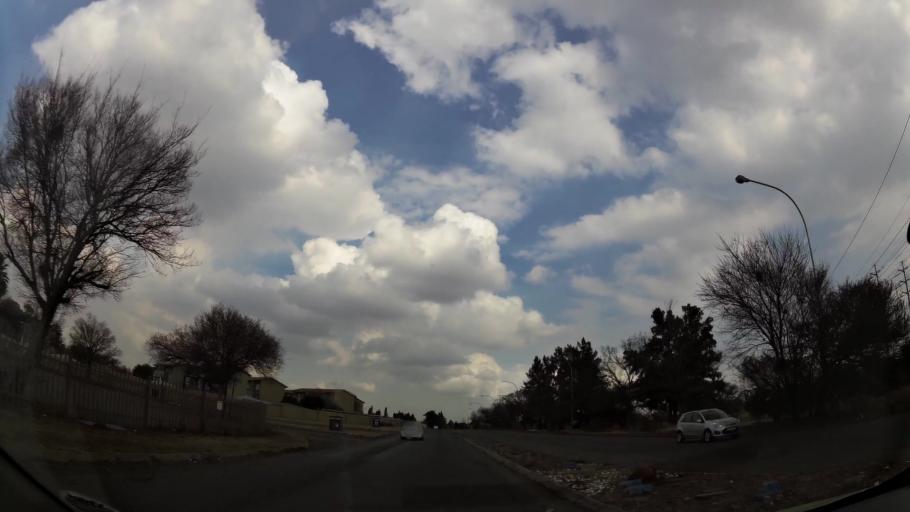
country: ZA
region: Gauteng
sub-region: Sedibeng District Municipality
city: Vereeniging
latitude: -26.6706
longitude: 27.9392
